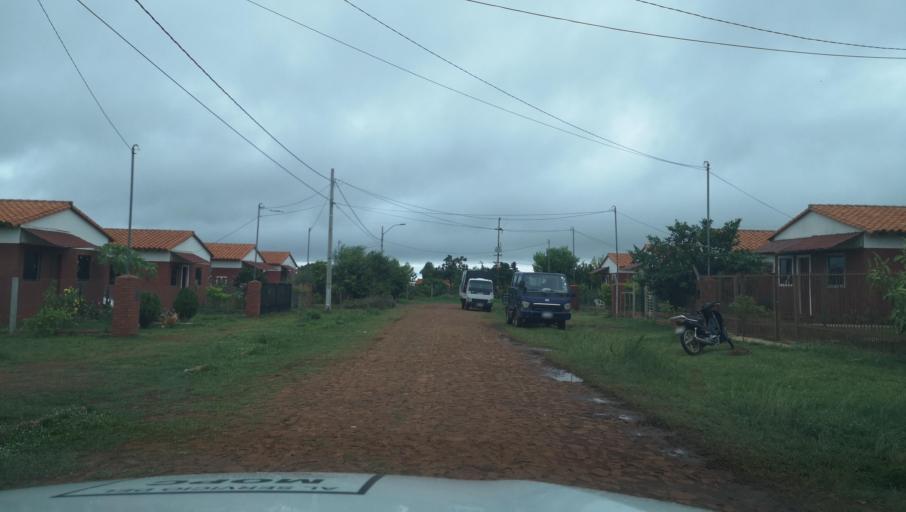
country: PY
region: Misiones
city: Santa Maria
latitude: -26.9022
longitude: -57.0385
